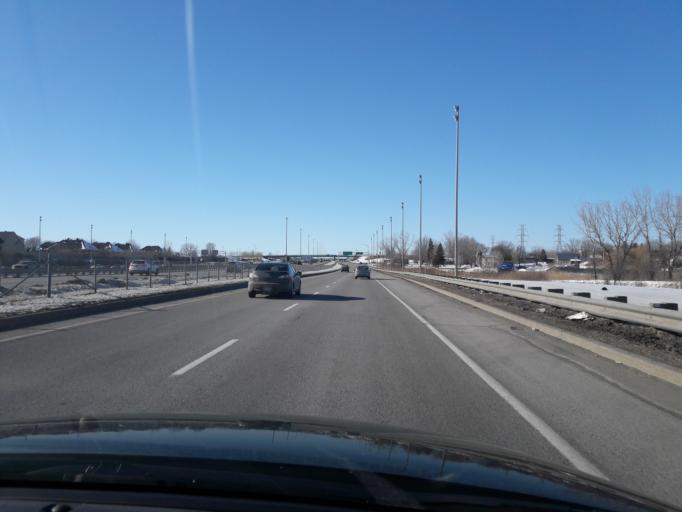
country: CA
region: Quebec
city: Dollard-Des Ormeaux
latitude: 45.5192
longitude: -73.7718
